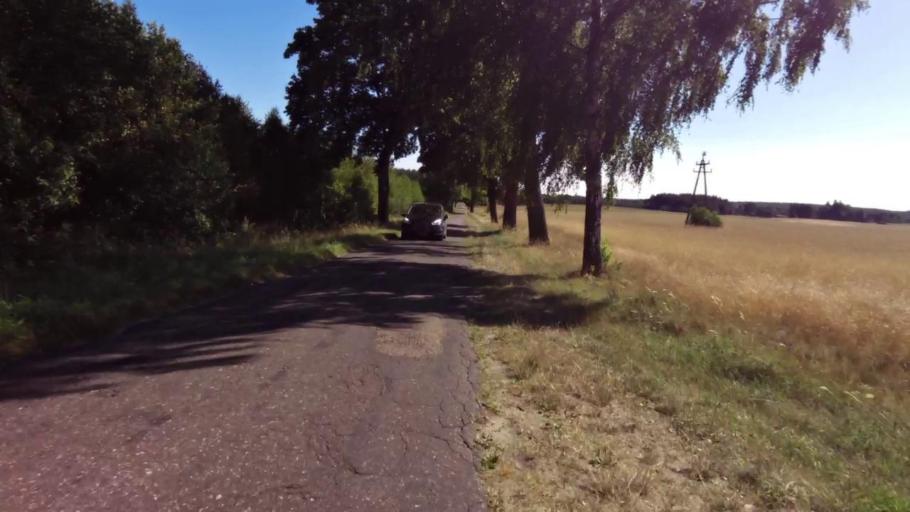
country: PL
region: West Pomeranian Voivodeship
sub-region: Powiat szczecinecki
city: Szczecinek
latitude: 53.7910
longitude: 16.6777
